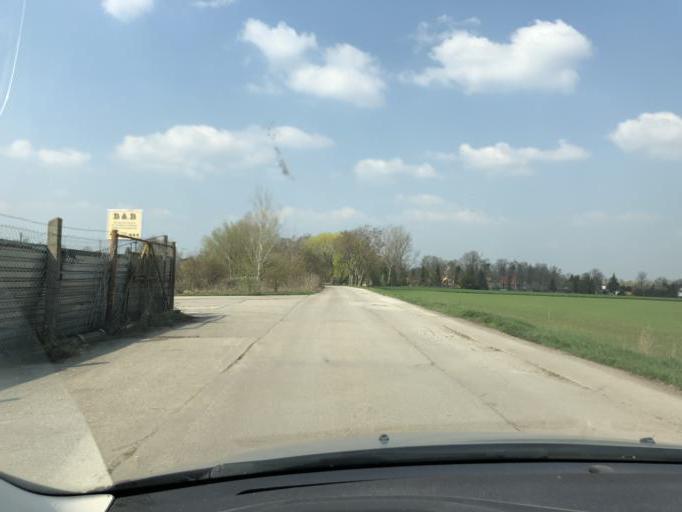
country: DE
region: Saxony-Anhalt
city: Landsberg
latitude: 51.5460
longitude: 12.1380
